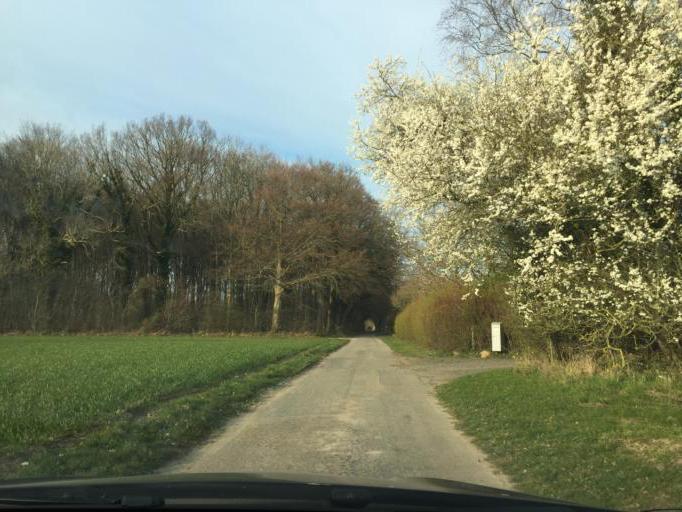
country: DK
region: South Denmark
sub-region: Kerteminde Kommune
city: Langeskov
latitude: 55.3323
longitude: 10.5881
